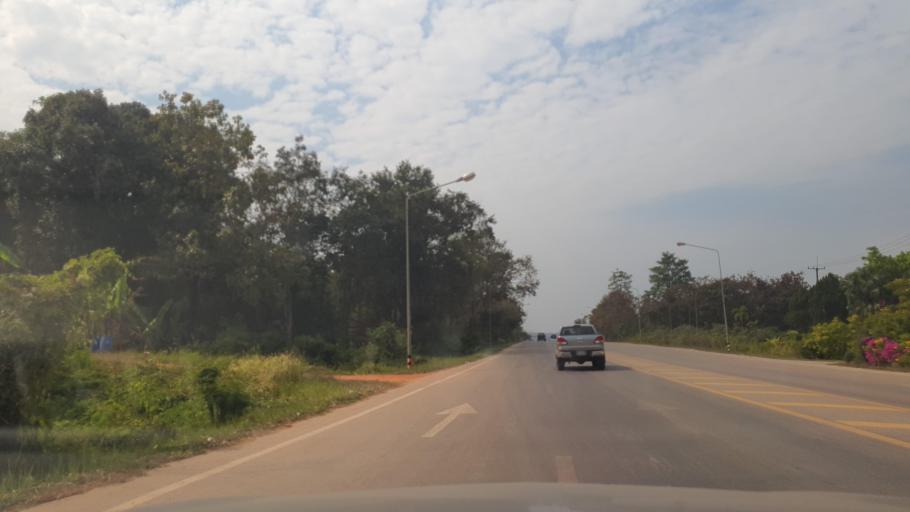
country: TH
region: Changwat Bueng Kan
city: Bung Khla
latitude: 18.2774
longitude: 103.8611
